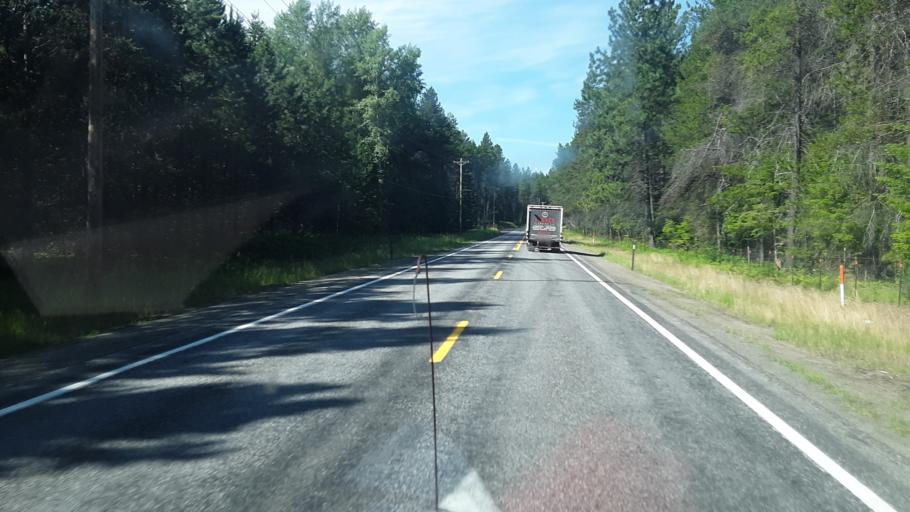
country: US
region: Idaho
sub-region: Boundary County
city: Bonners Ferry
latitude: 48.5295
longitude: -116.4294
